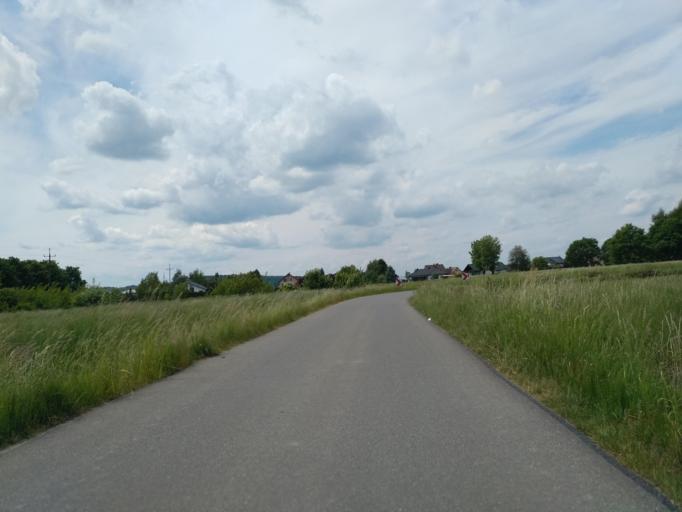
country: PL
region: Subcarpathian Voivodeship
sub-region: Powiat krosnienski
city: Chorkowka
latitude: 49.6839
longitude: 21.7031
